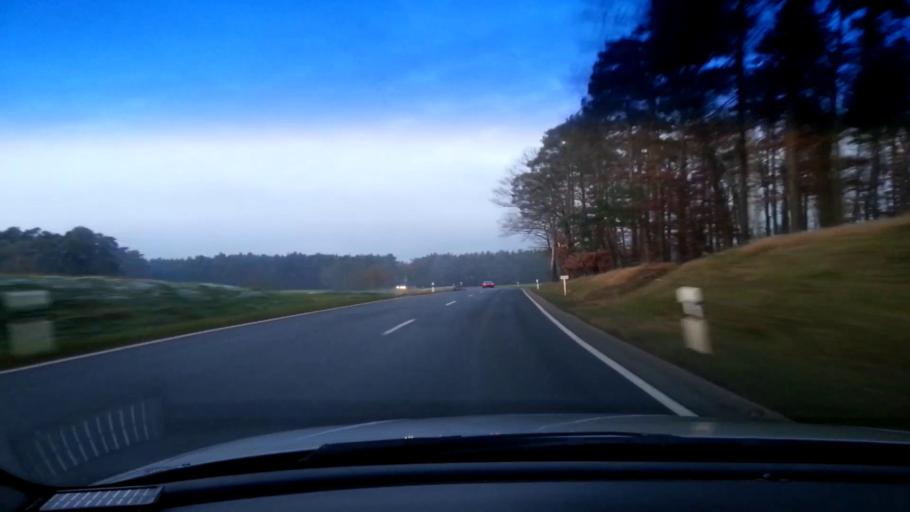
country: DE
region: Bavaria
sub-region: Upper Franconia
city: Pommersfelden
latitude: 49.7949
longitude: 10.8266
